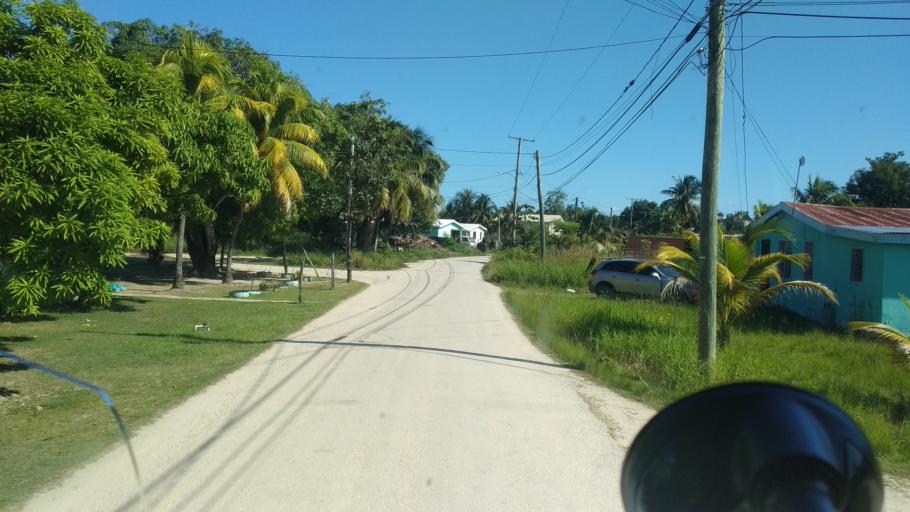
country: BZ
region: Belize
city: Belize City
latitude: 17.5559
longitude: -88.3039
